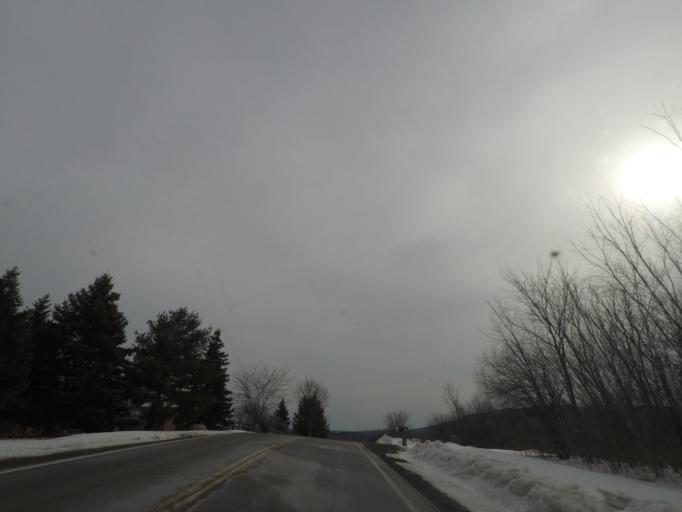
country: US
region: New York
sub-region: Albany County
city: Altamont
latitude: 42.6779
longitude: -73.9817
